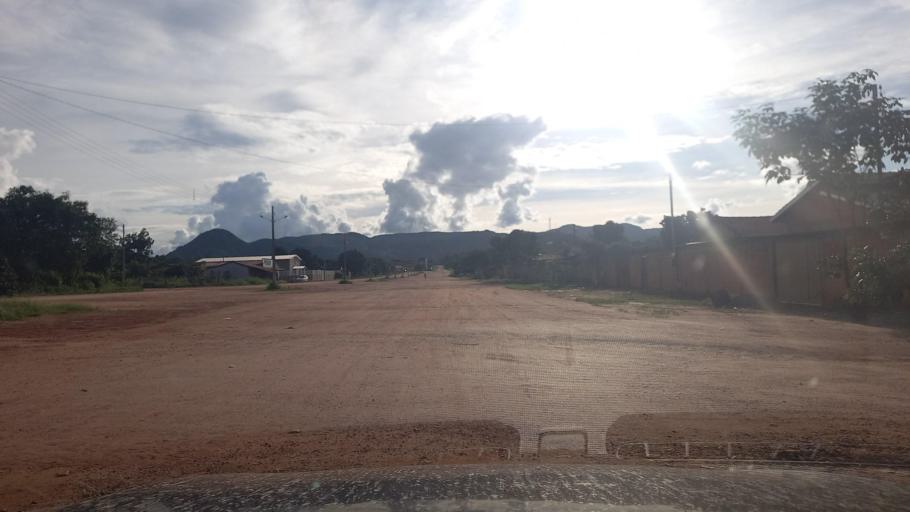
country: BR
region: Goias
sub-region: Cavalcante
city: Cavalcante
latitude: -13.7974
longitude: -47.4422
